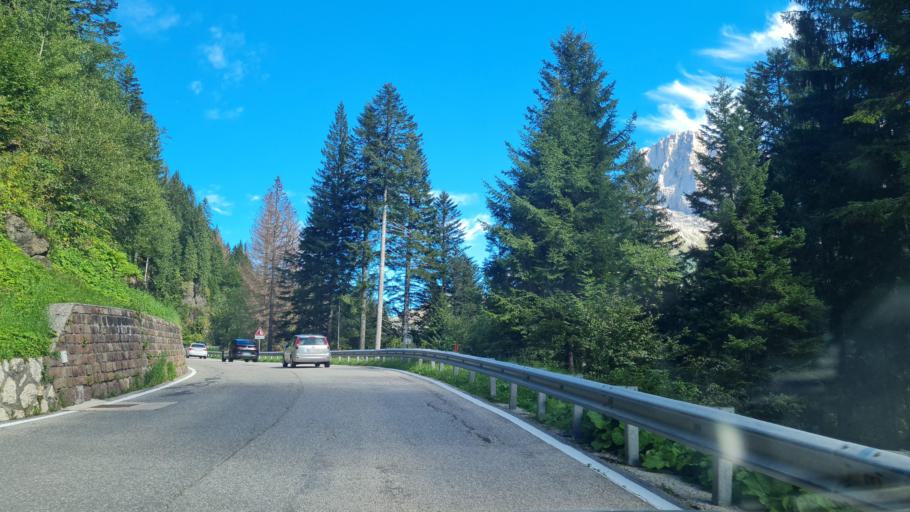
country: IT
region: Trentino-Alto Adige
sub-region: Provincia di Trento
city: Siror
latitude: 46.2452
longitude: 11.8043
